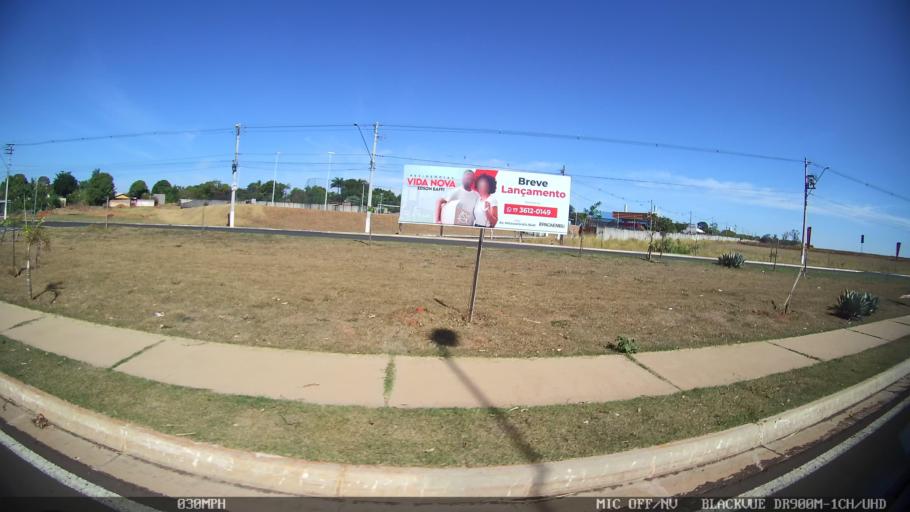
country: BR
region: Sao Paulo
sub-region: Sao Jose Do Rio Preto
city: Sao Jose do Rio Preto
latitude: -20.7579
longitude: -49.4370
